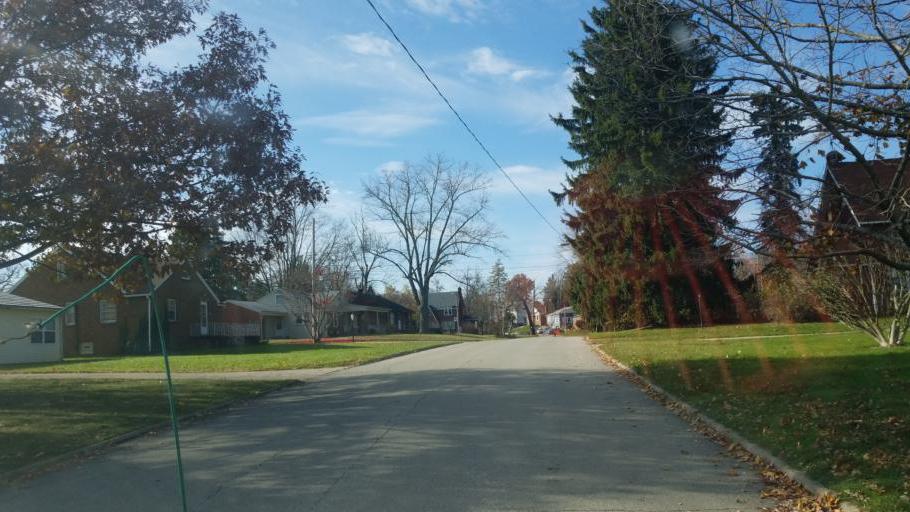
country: US
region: Ohio
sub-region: Richland County
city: Mansfield
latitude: 40.7275
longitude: -82.5374
